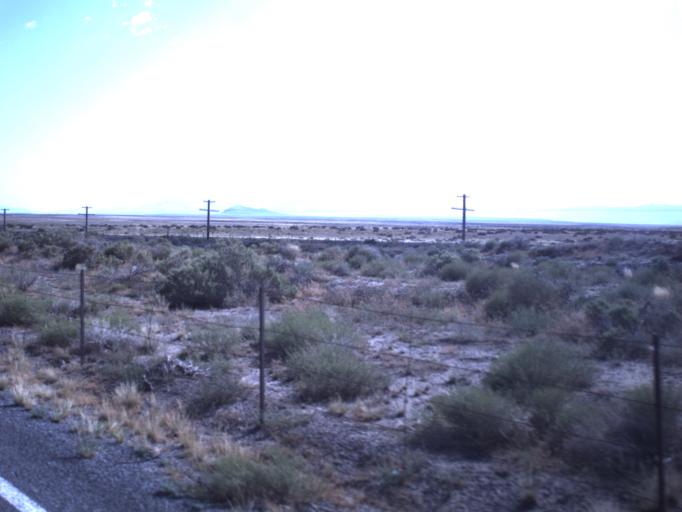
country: US
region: Utah
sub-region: Millard County
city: Delta
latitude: 38.9596
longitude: -112.8036
